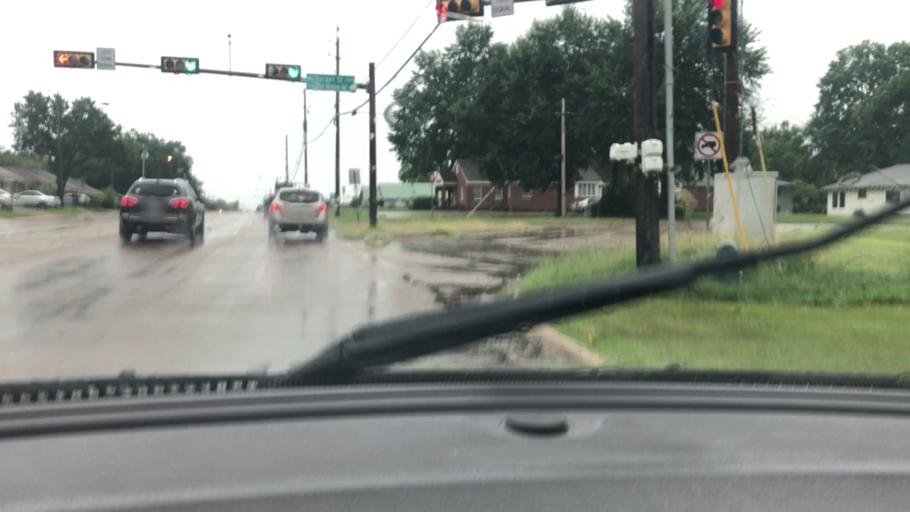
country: US
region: Texas
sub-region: Bowie County
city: Wake Village
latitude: 33.4412
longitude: -94.0804
